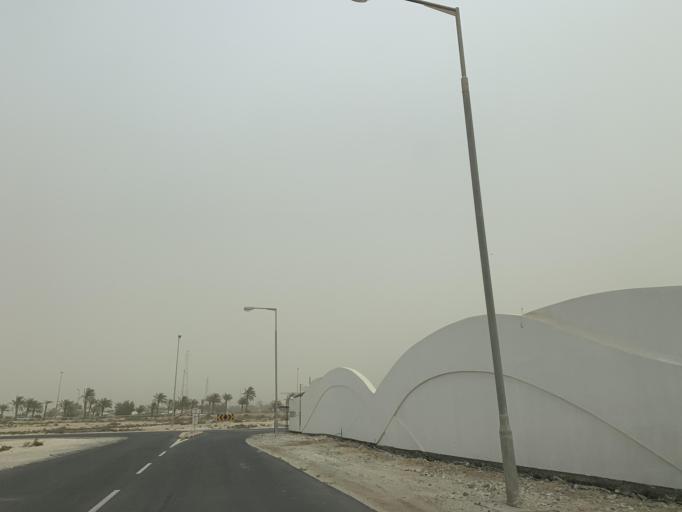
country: BH
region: Northern
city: Ar Rifa'
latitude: 26.1441
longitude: 50.5380
